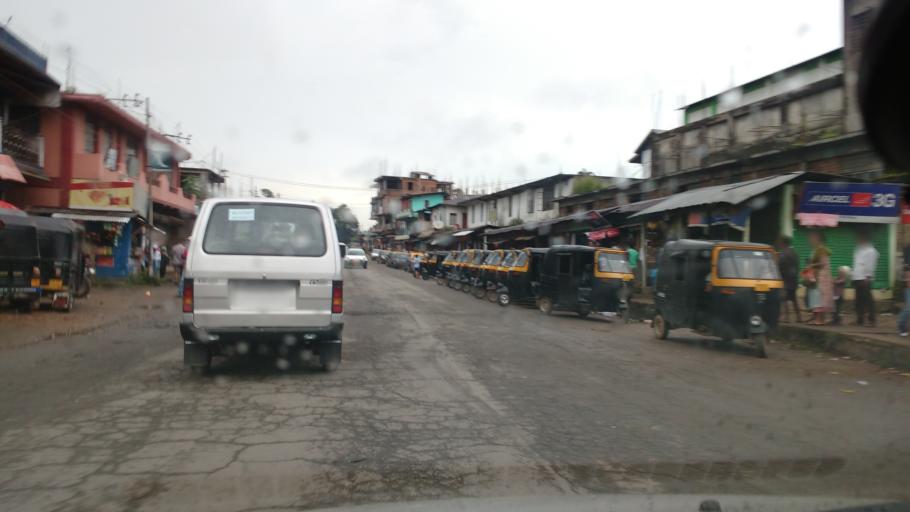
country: IN
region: Meghalaya
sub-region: Ri-Bhoi
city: Nongpoh
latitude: 25.7498
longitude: 91.8871
